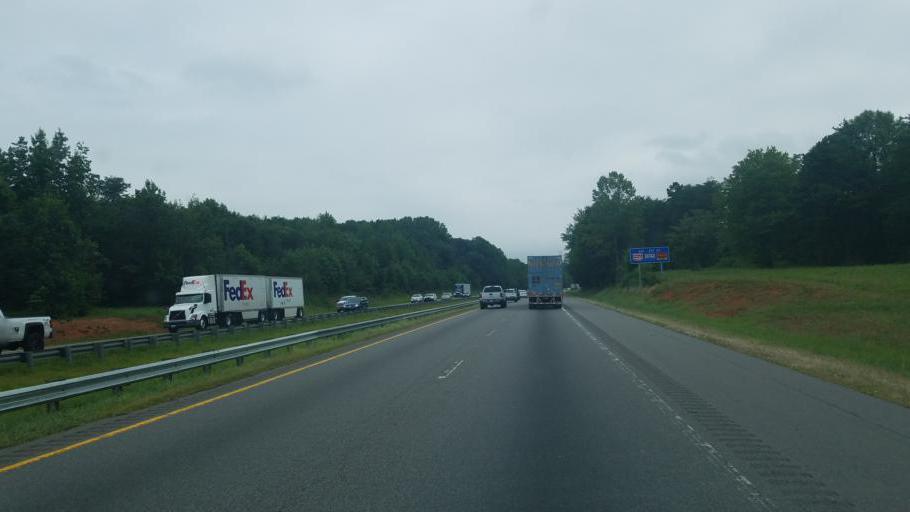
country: US
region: North Carolina
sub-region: Iredell County
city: Troutman
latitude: 35.6637
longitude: -80.8599
